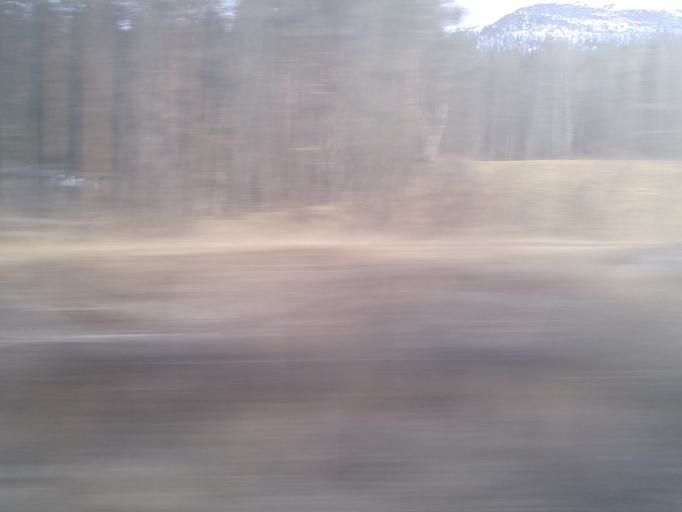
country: NO
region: Oppland
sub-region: Dovre
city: Dovre
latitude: 61.8951
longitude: 9.3960
